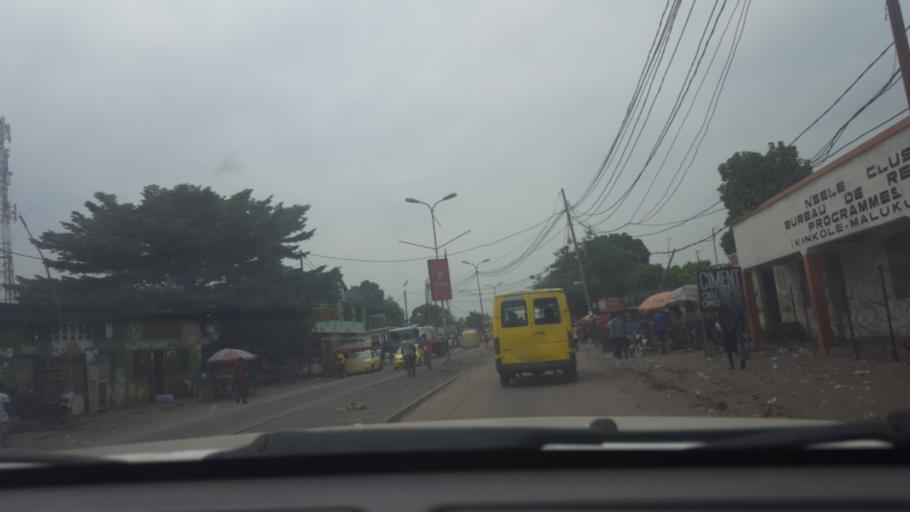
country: CD
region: Kinshasa
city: Masina
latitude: -4.3237
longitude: 15.5144
